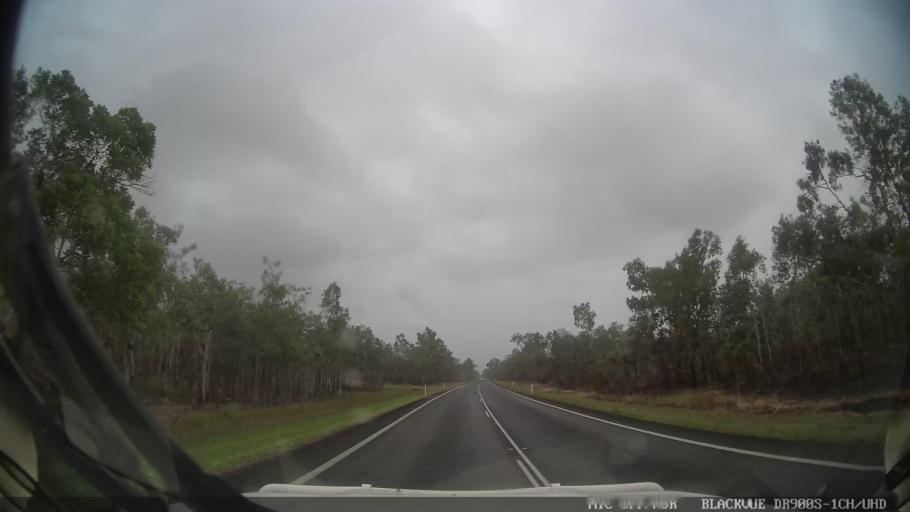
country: AU
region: Queensland
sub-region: Hinchinbrook
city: Ingham
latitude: -18.4374
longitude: 146.1391
